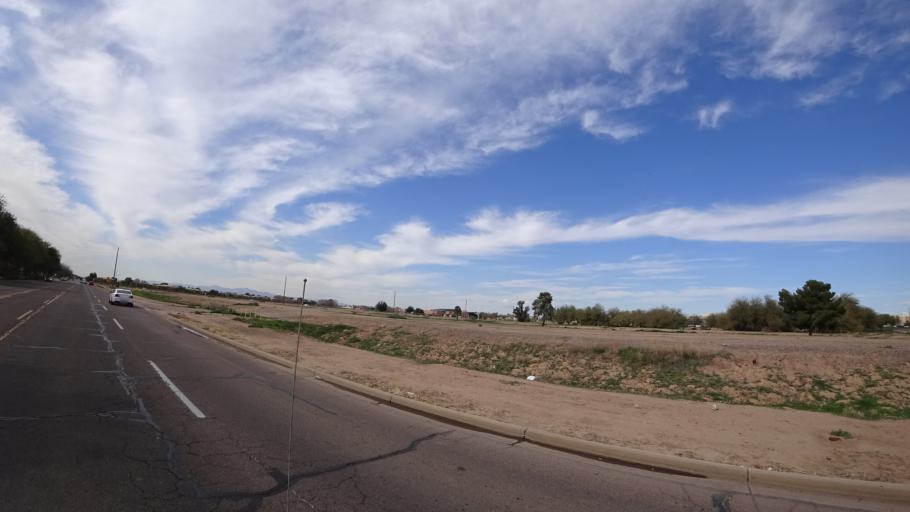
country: US
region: Arizona
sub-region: Maricopa County
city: Tolleson
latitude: 33.4728
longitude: -112.2266
